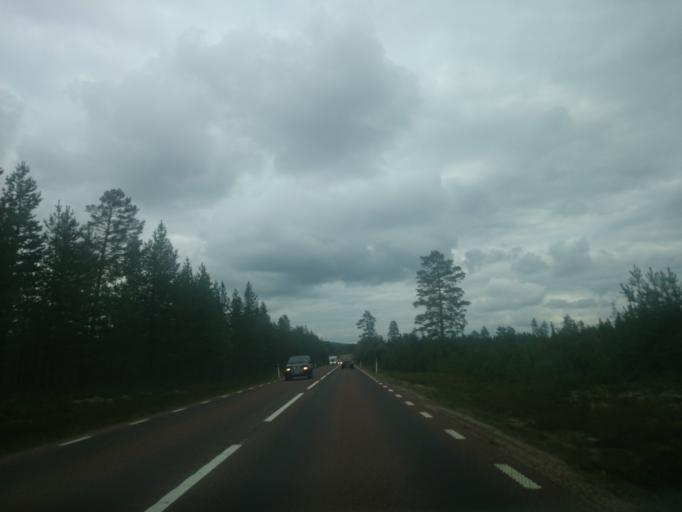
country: SE
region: Jaemtland
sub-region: Harjedalens Kommun
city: Sveg
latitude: 62.0426
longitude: 14.4678
